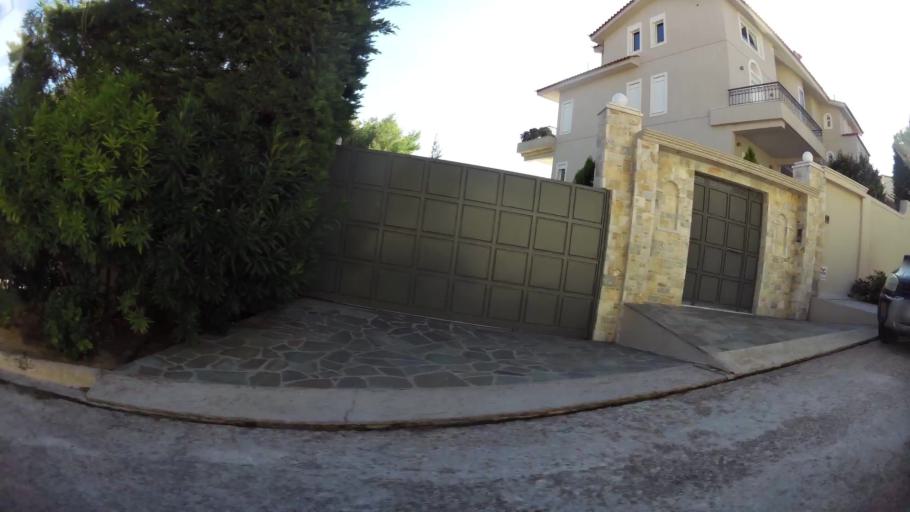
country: GR
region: Attica
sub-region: Nomarchia Anatolikis Attikis
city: Dhrafi
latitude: 38.0178
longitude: 23.8978
